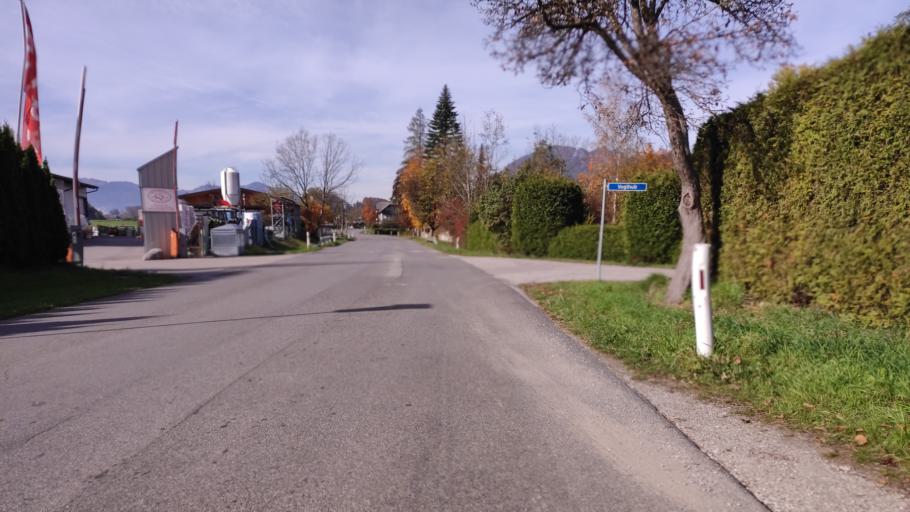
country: AT
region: Salzburg
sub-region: Politischer Bezirk Salzburg-Umgebung
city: Strobl
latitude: 47.7140
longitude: 13.5405
